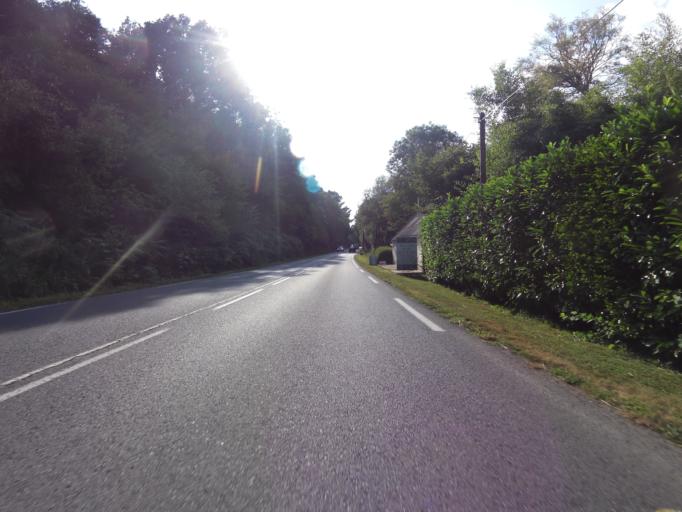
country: FR
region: Brittany
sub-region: Departement du Finistere
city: Pouldreuzic
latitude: 47.9702
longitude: -4.3759
